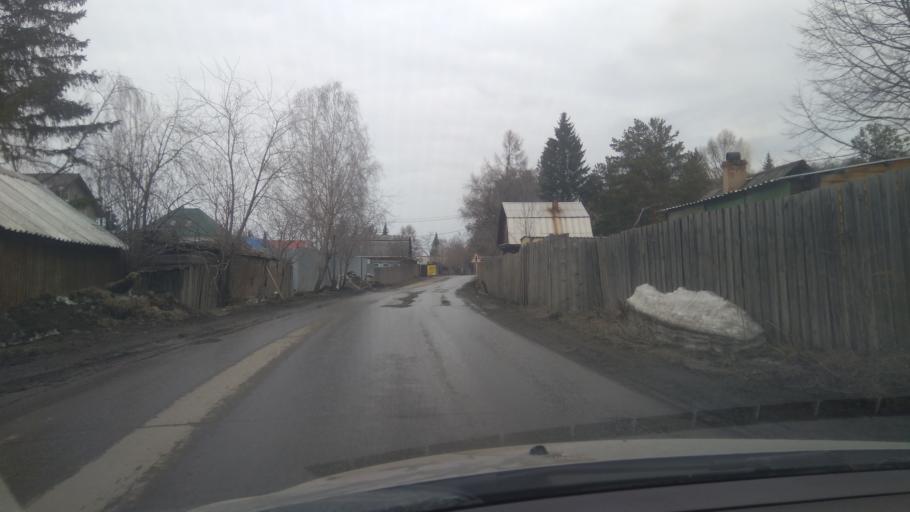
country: RU
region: Sverdlovsk
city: Severka
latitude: 56.8482
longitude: 60.3835
